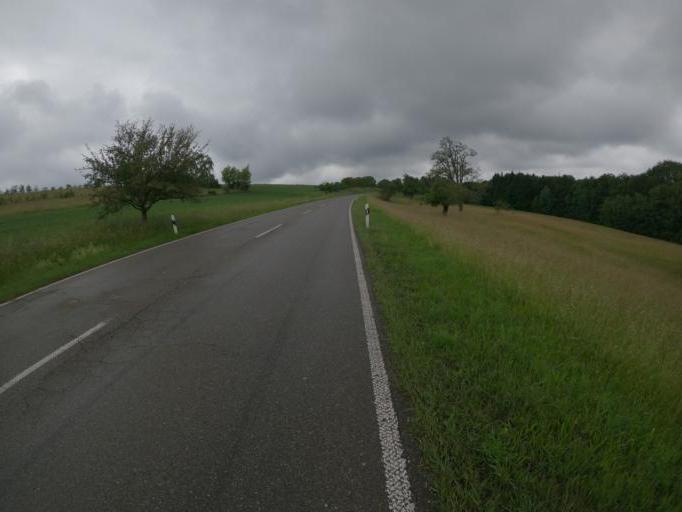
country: DE
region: Baden-Wuerttemberg
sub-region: Regierungsbezirk Stuttgart
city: Adelberg
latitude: 48.7538
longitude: 9.6078
